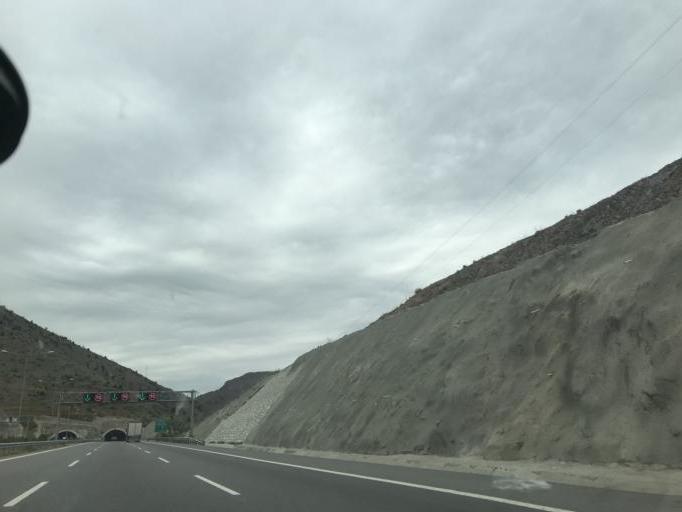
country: TR
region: Nigde
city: Ciftehan
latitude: 37.5707
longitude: 34.7541
